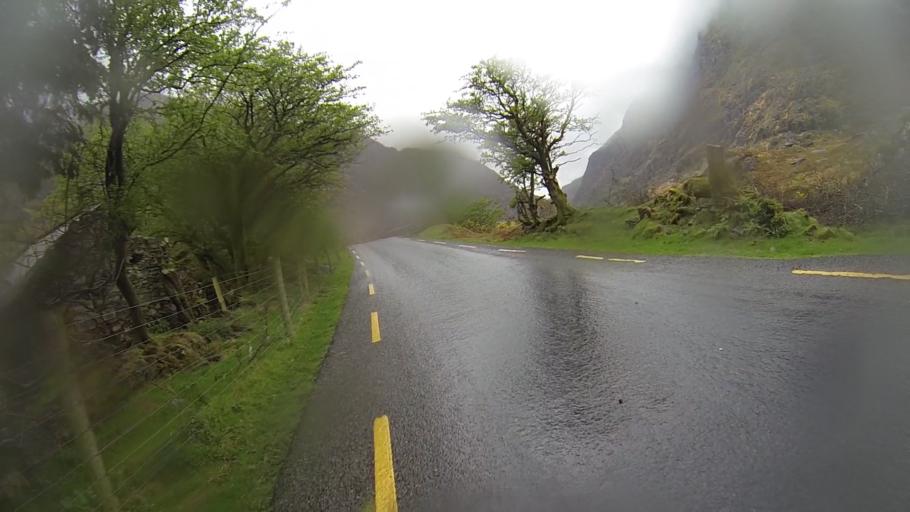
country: IE
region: Munster
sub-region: Ciarrai
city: Cill Airne
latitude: 52.0168
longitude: -9.6358
